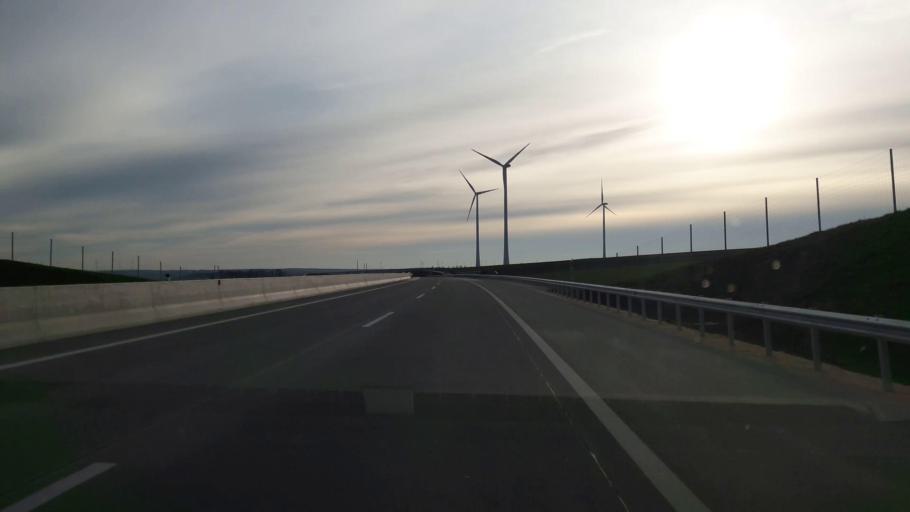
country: AT
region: Lower Austria
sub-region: Politischer Bezirk Mistelbach
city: Grosskrut
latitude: 48.6283
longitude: 16.6765
